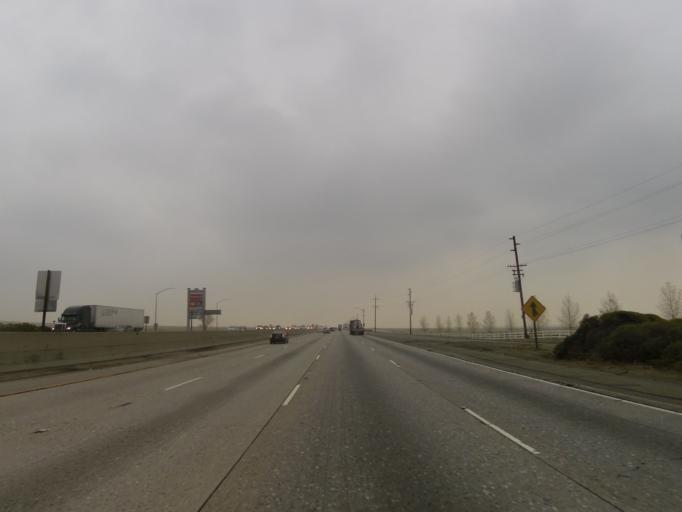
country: US
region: California
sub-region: Kern County
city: Frazier Park
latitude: 34.9430
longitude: -118.9315
